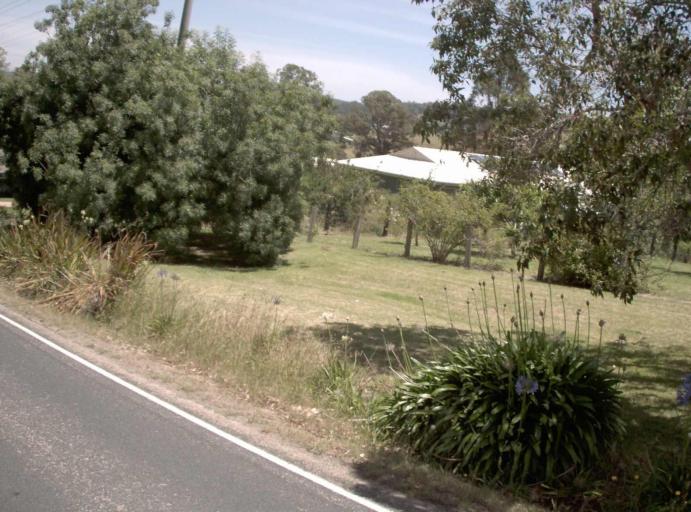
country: AU
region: Victoria
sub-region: East Gippsland
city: Lakes Entrance
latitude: -37.7012
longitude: 147.8352
